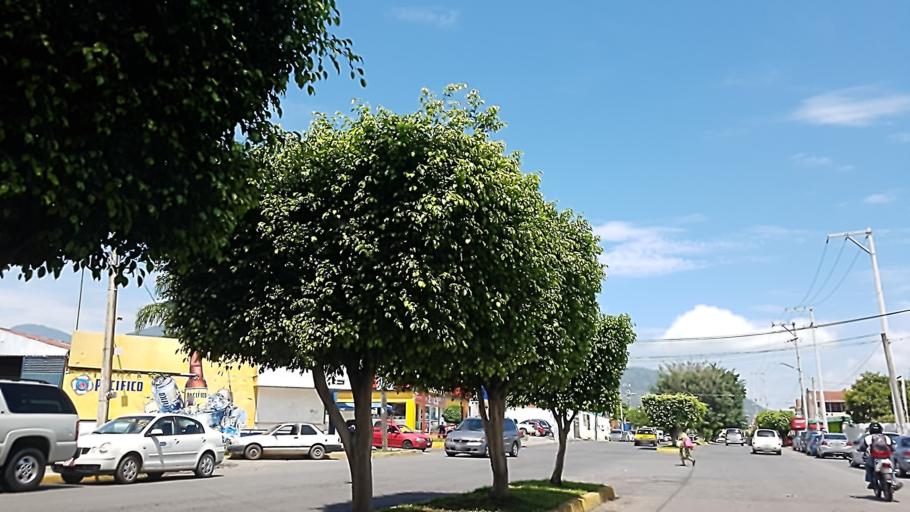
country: MX
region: Nayarit
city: Tepic
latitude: 21.4848
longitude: -104.8819
